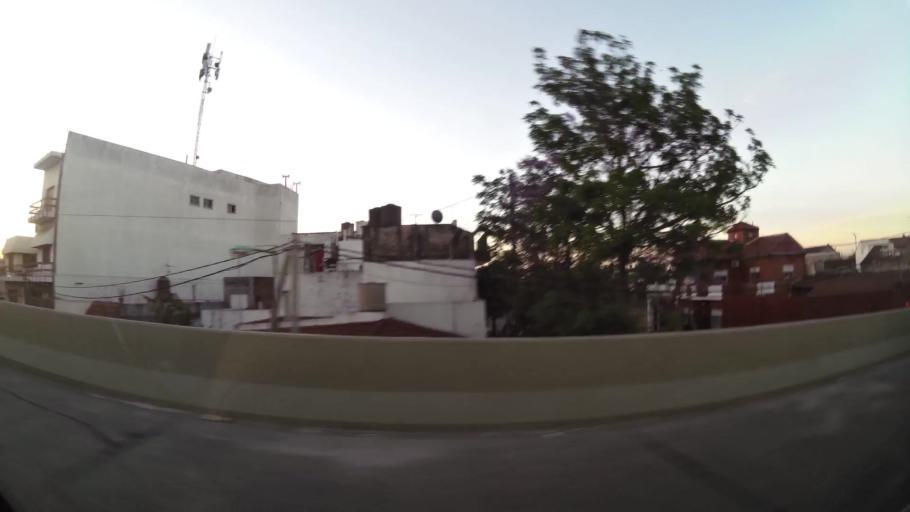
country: AR
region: Buenos Aires F.D.
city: Villa Lugano
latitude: -34.6732
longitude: -58.4710
